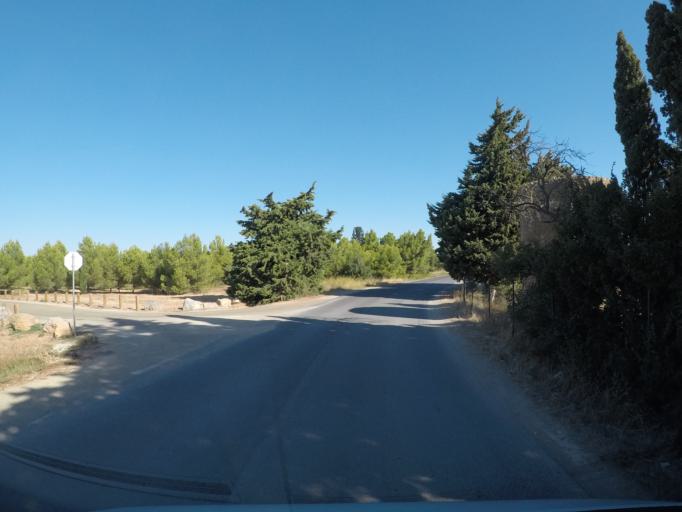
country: FR
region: Languedoc-Roussillon
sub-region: Departement de l'Aude
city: Narbonne
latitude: 43.1444
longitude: 3.0033
